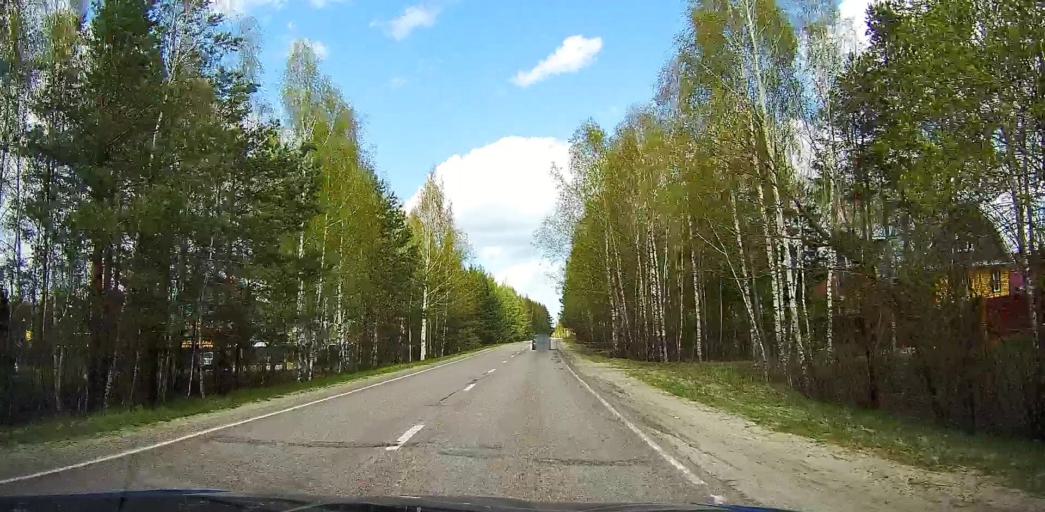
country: RU
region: Moskovskaya
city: Davydovo
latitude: 55.5899
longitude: 38.8317
